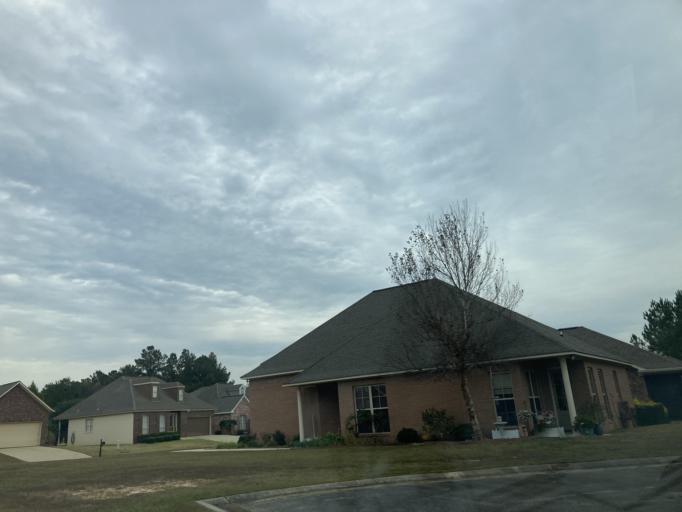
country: US
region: Mississippi
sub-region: Lamar County
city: West Hattiesburg
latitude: 31.3216
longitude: -89.3970
